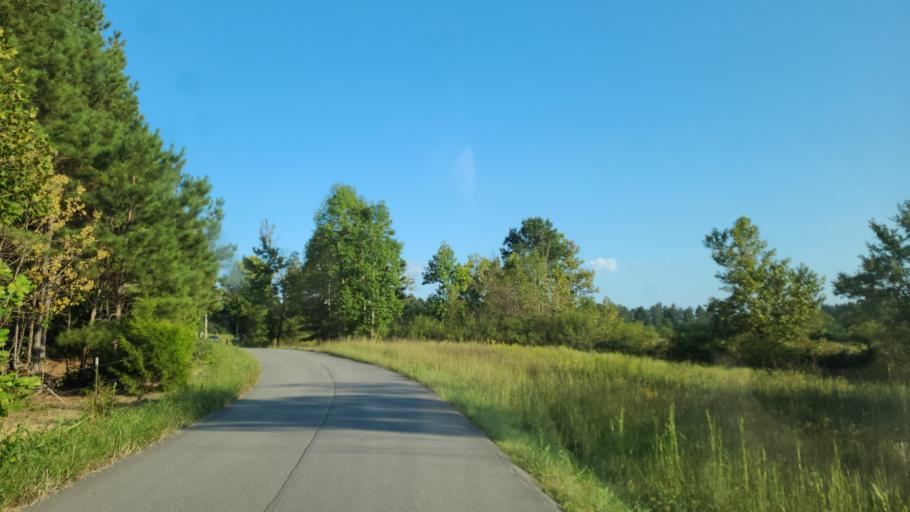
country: US
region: Tennessee
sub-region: Bradley County
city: Wildwood Lake
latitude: 35.0235
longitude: -84.7714
